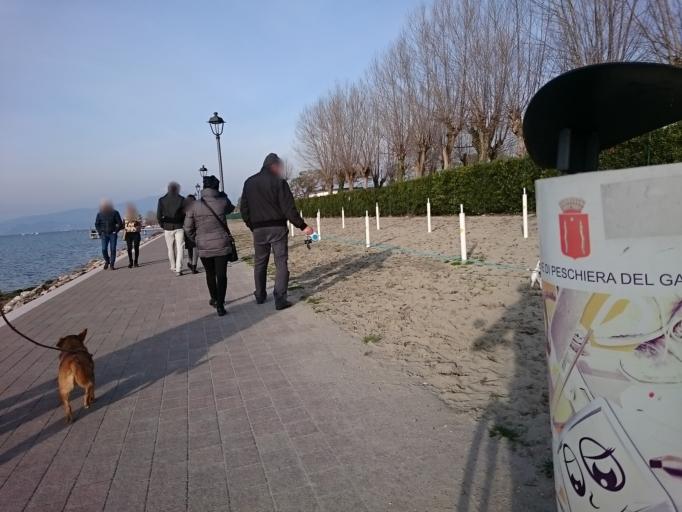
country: IT
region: Veneto
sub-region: Provincia di Verona
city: Peschiera del Garda
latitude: 45.4484
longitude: 10.6955
